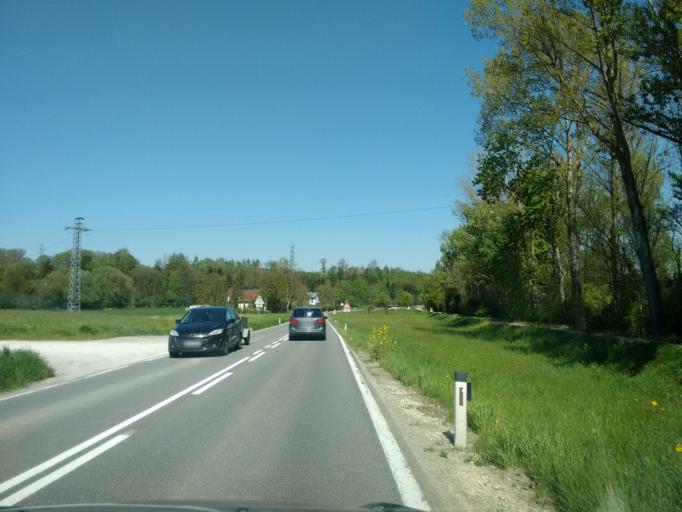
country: AT
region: Upper Austria
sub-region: Politischer Bezirk Steyr-Land
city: Bad Hall
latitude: 48.0463
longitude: 14.2070
